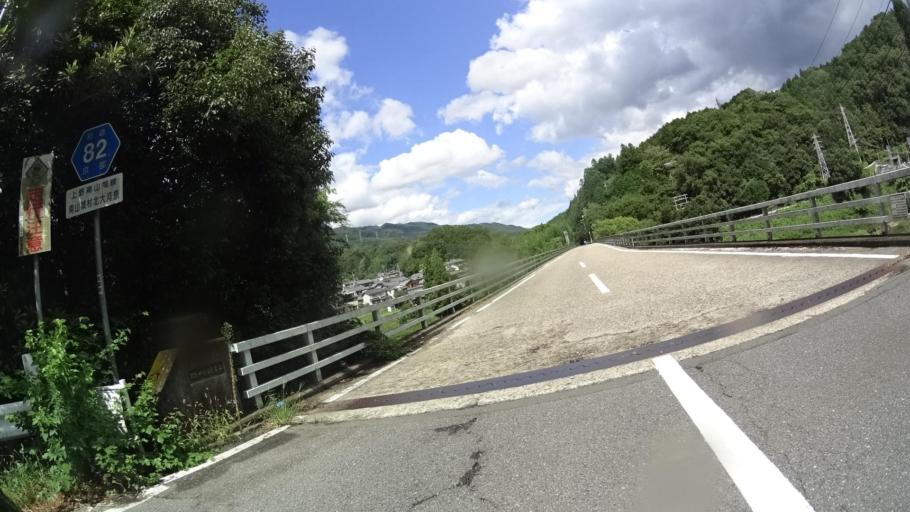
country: JP
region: Mie
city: Ueno-ebisumachi
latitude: 34.7694
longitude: 135.9975
